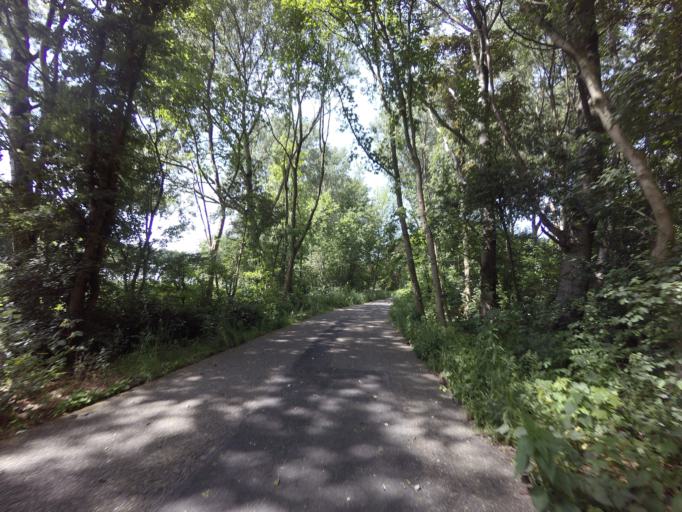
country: NL
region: North Holland
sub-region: Gemeente Zaanstad
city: Zaanstad
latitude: 52.3939
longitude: 4.7386
